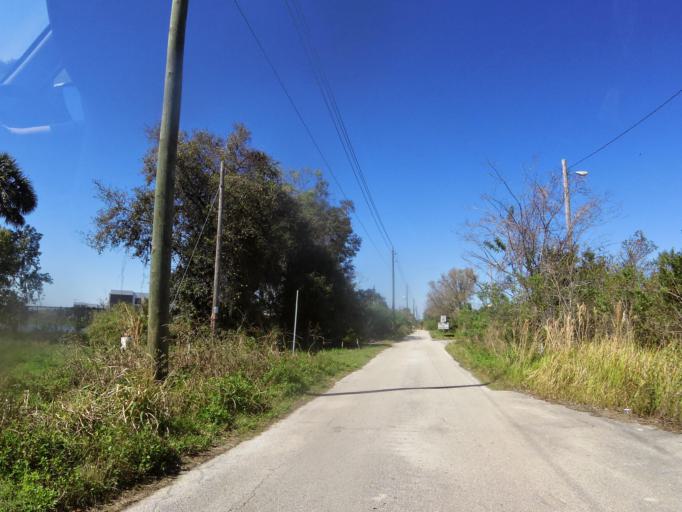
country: US
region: Florida
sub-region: Seminole County
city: Sanford
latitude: 28.8179
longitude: -81.3061
